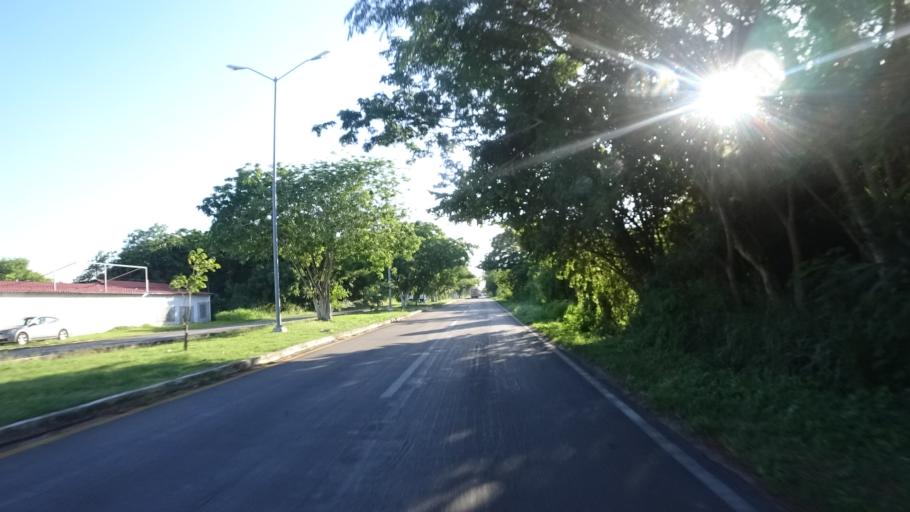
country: MX
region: Campeche
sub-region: Campeche
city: Campeche
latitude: 19.8861
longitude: -90.4733
